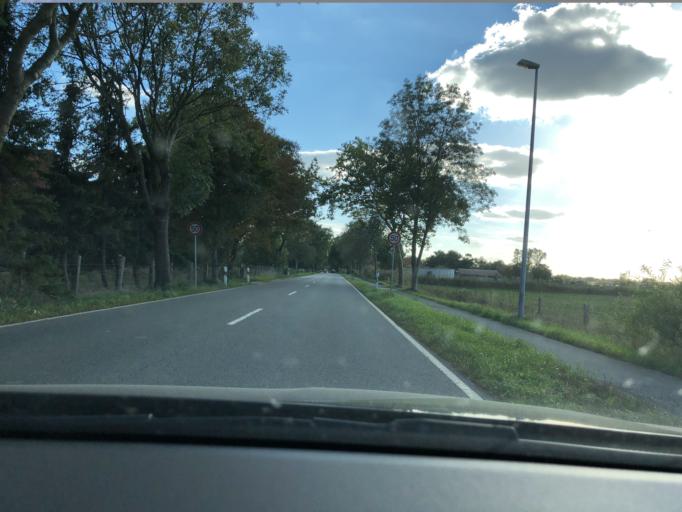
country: DE
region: Lower Saxony
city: Stuhr
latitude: 53.0348
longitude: 8.7601
